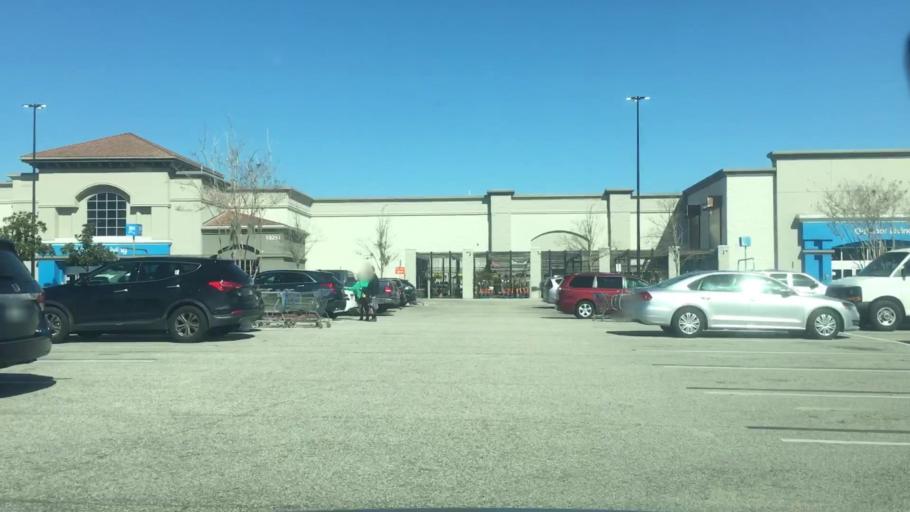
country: US
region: Florida
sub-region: Saint Johns County
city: Fruit Cove
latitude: 30.1779
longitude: -81.5566
